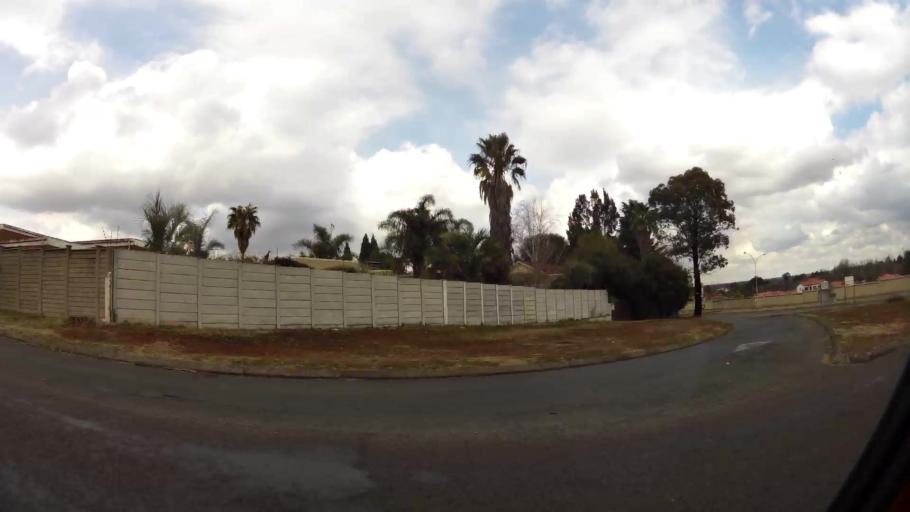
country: ZA
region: Gauteng
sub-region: Sedibeng District Municipality
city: Vanderbijlpark
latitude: -26.7347
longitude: 27.8428
